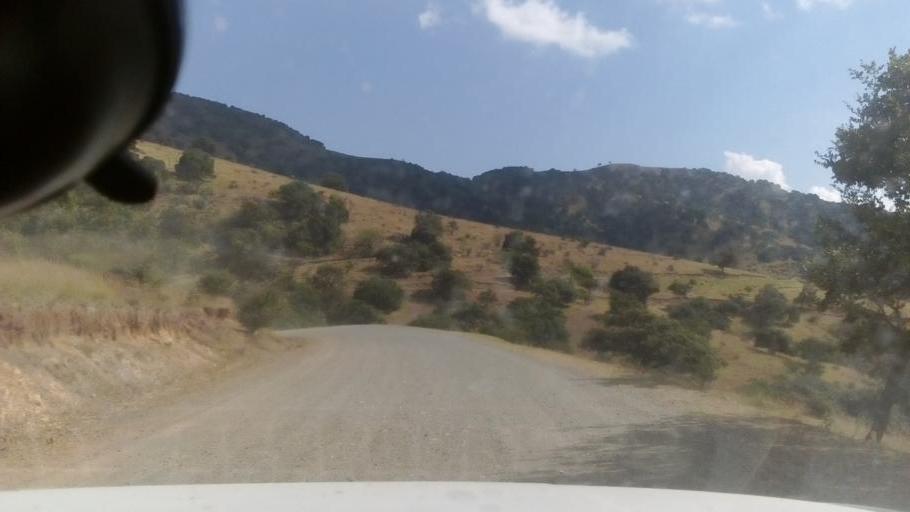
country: MX
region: Guanajuato
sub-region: Leon
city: Lucio Blanco (Los Gavilanes)
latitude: 21.2050
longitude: -101.5032
